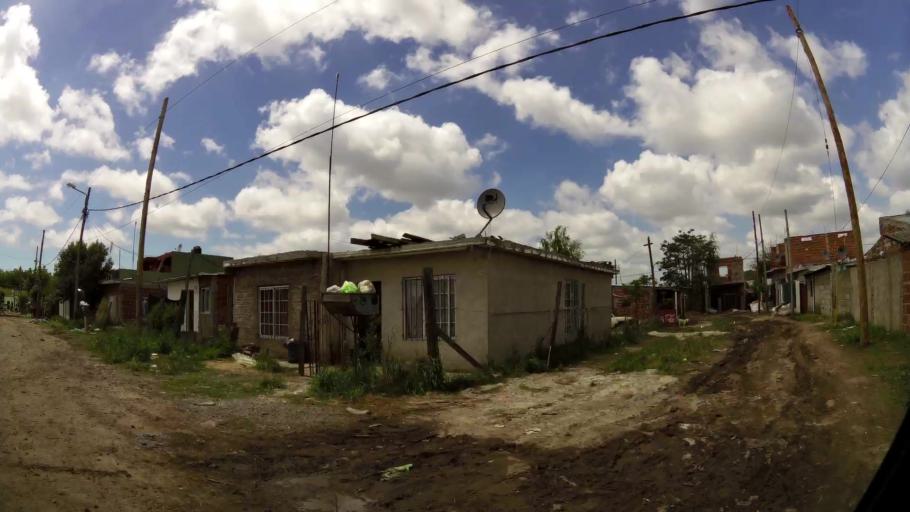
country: AR
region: Buenos Aires
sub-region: Partido de Quilmes
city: Quilmes
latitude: -34.8223
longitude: -58.2443
